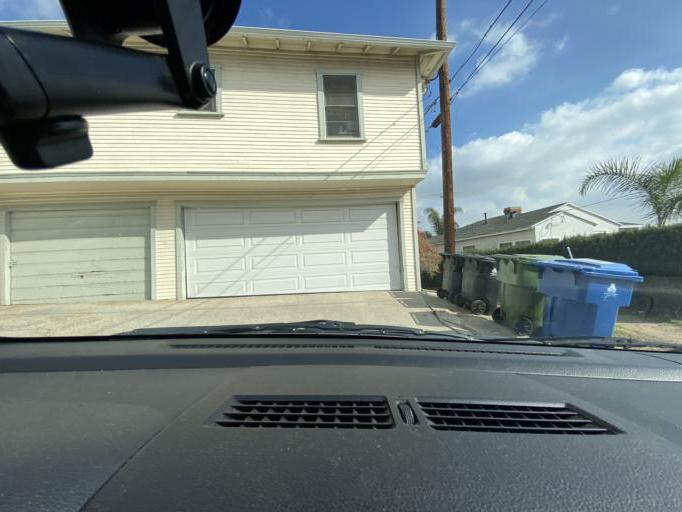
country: US
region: California
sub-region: Los Angeles County
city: Culver City
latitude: 34.0173
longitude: -118.4186
